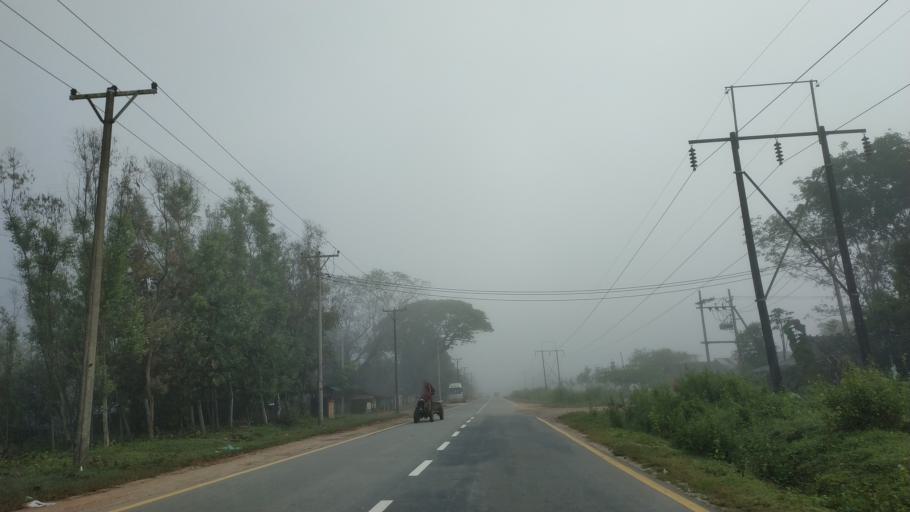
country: MM
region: Tanintharyi
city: Dawei
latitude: 14.1715
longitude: 98.2089
